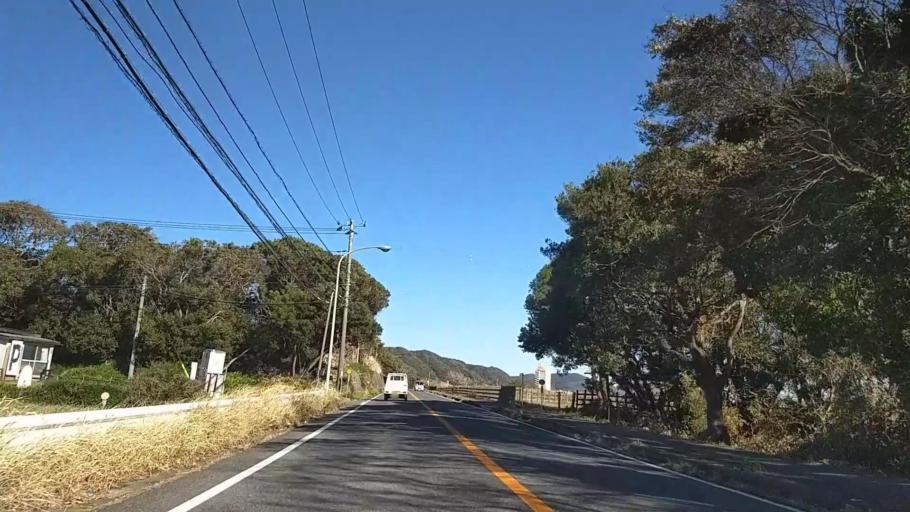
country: JP
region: Chiba
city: Kawaguchi
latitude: 35.0453
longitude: 140.0246
